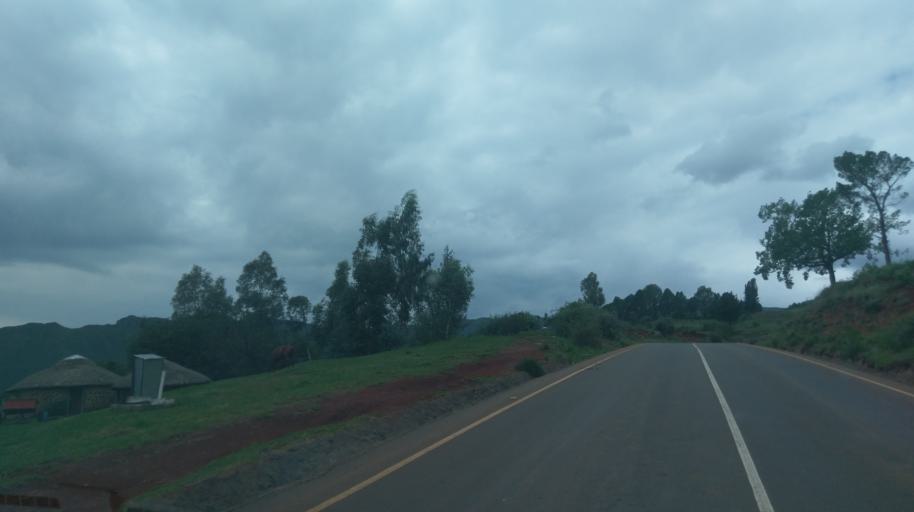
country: LS
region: Butha-Buthe
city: Butha-Buthe
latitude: -29.0361
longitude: 28.2812
